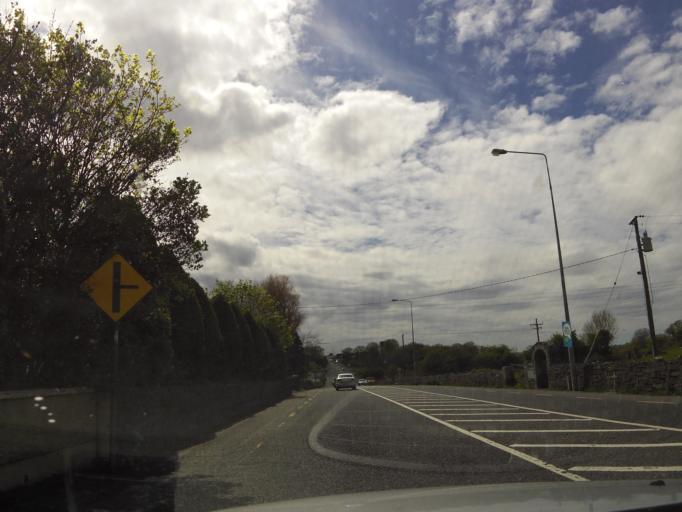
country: IE
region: Connaught
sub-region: County Galway
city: Gaillimh
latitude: 53.2970
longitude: -9.0129
